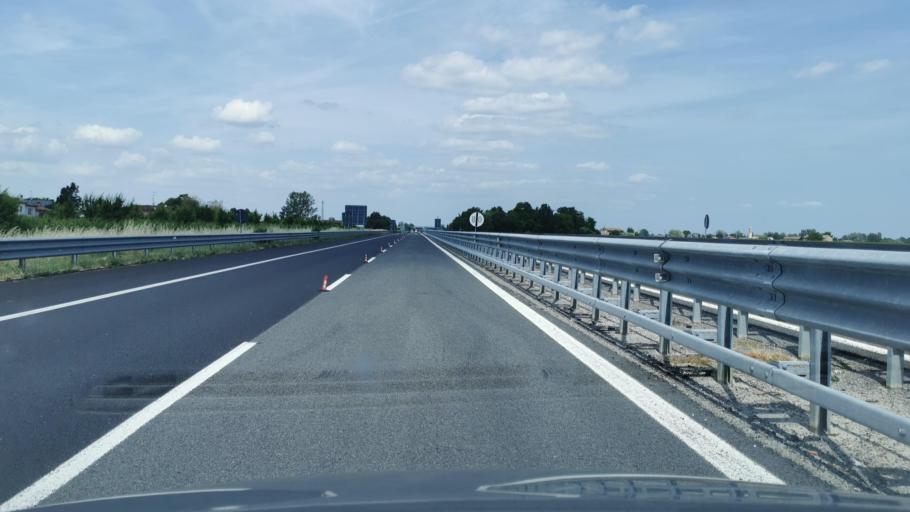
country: IT
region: Emilia-Romagna
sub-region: Provincia di Ravenna
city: Solarolo
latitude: 44.3588
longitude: 11.8214
